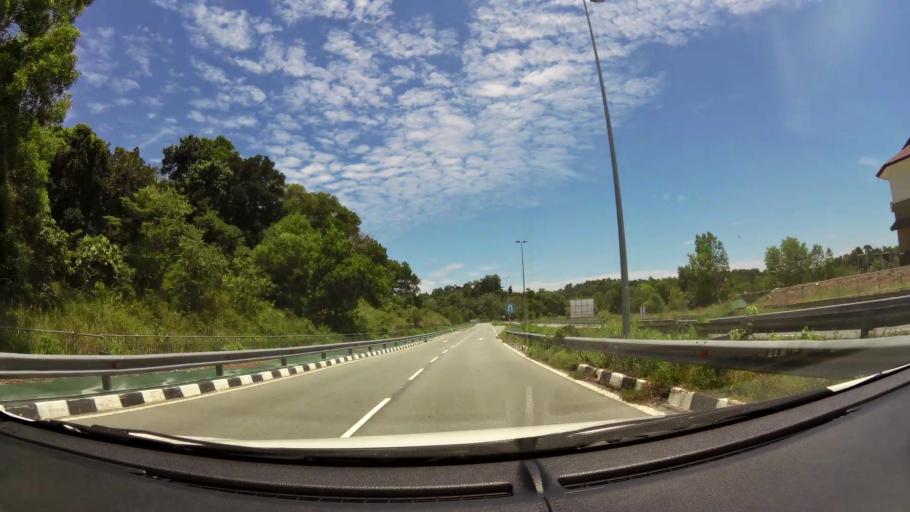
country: BN
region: Brunei and Muara
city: Bandar Seri Begawan
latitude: 5.0076
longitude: 115.0036
